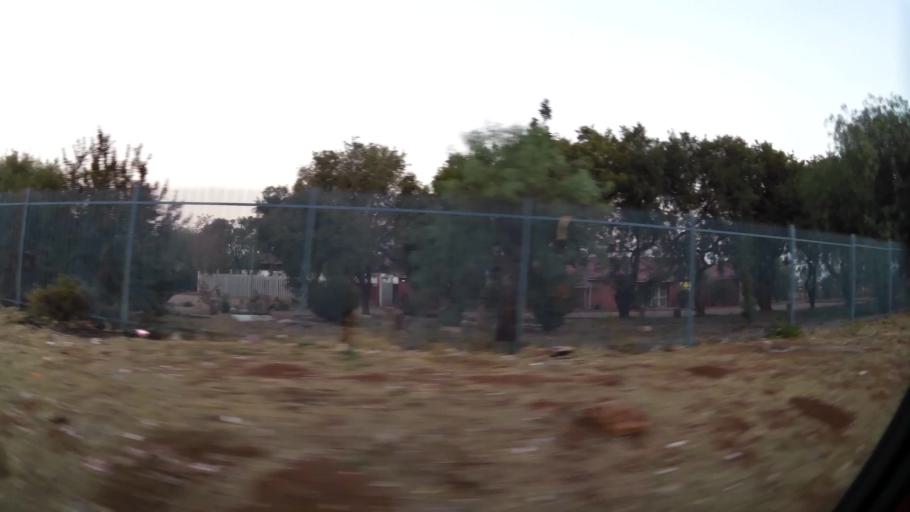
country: ZA
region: Gauteng
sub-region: City of Johannesburg Metropolitan Municipality
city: Soweto
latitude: -26.2910
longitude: 27.8733
